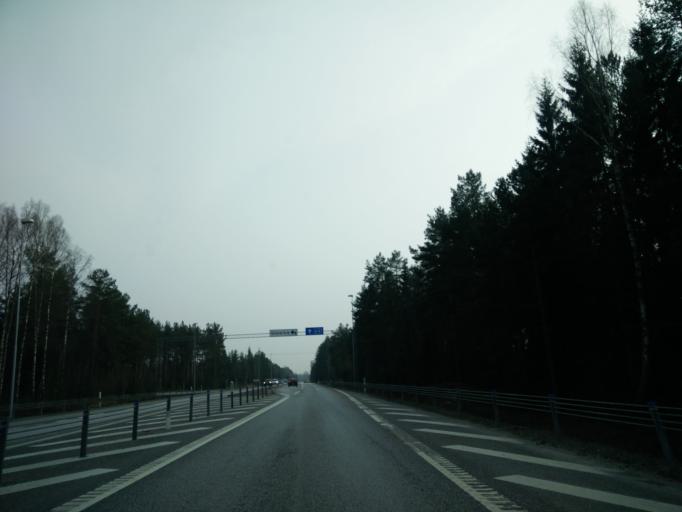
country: SE
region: Vaermland
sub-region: Forshaga Kommun
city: Forshaga
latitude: 59.4564
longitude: 13.4166
